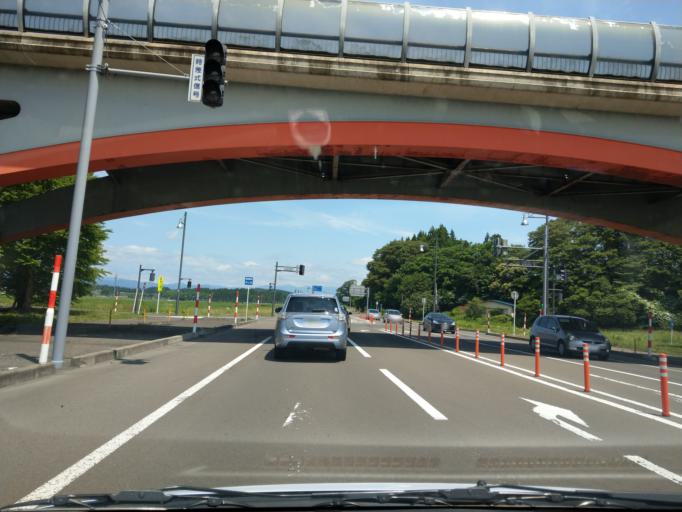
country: JP
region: Akita
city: Takanosu
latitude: 40.1880
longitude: 140.4005
